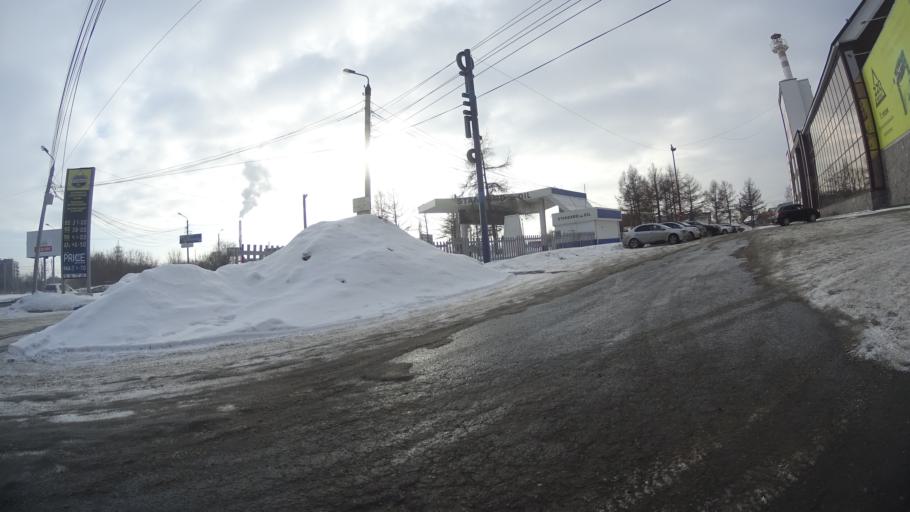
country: RU
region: Chelyabinsk
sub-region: Gorod Chelyabinsk
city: Chelyabinsk
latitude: 55.1187
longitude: 61.3861
